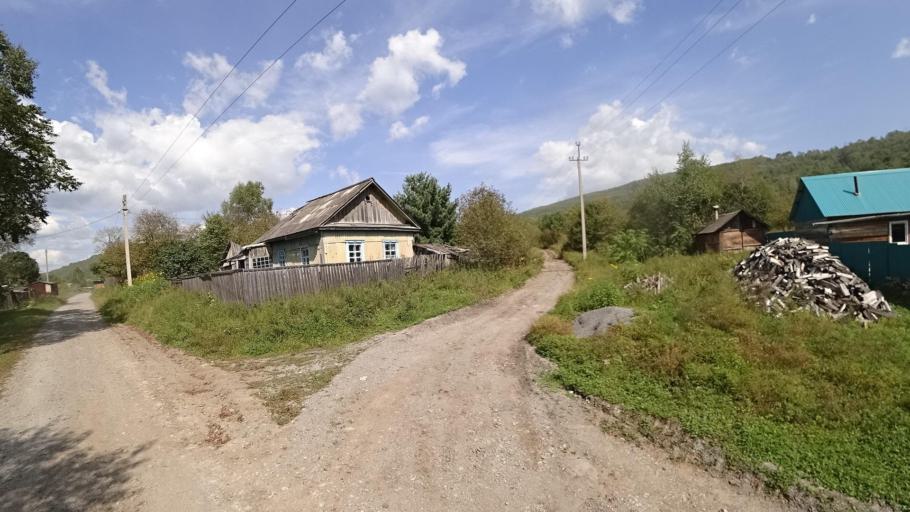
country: RU
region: Jewish Autonomous Oblast
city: Londoko
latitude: 49.0232
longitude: 131.9332
